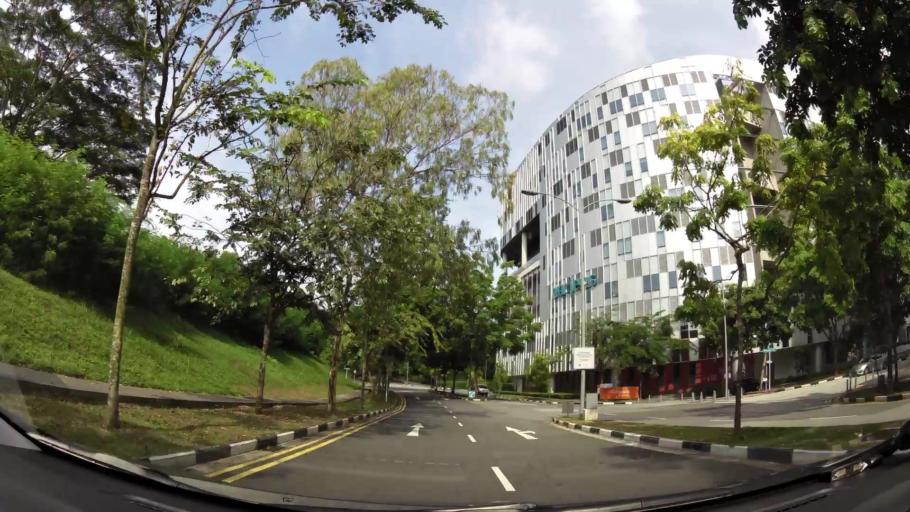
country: SG
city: Singapore
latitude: 1.3009
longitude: 103.7926
